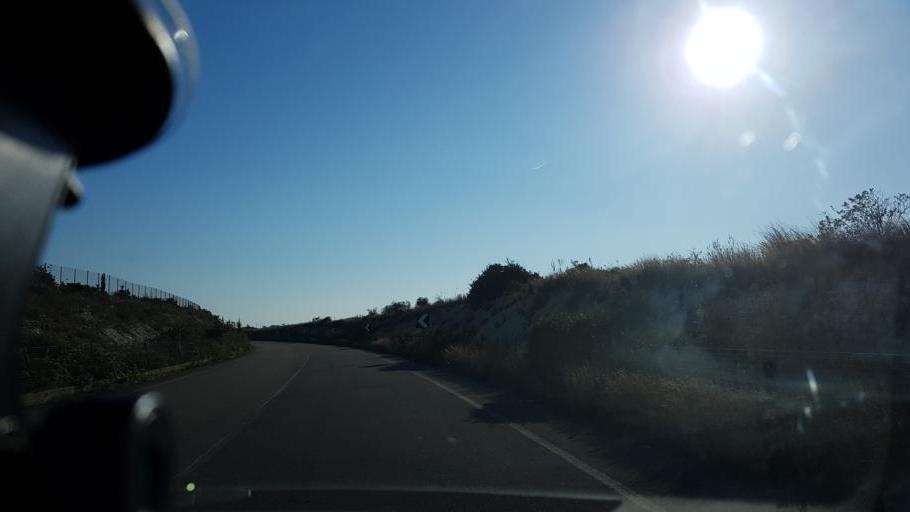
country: IT
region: Apulia
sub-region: Provincia di Lecce
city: Merine
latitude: 40.4059
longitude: 18.2512
